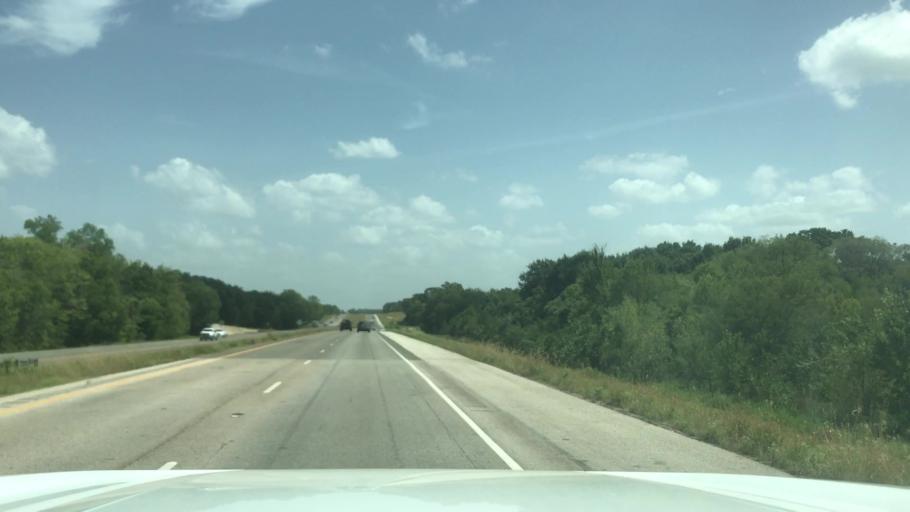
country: US
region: Texas
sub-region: Robertson County
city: Calvert
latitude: 30.9464
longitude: -96.6473
